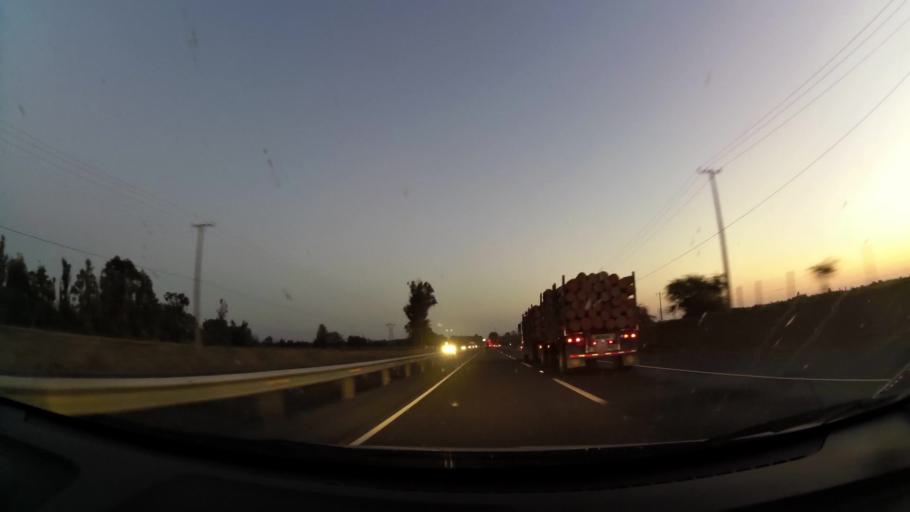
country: CL
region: Maule
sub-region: Provincia de Linares
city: Parral
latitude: -36.2079
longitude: -71.8221
